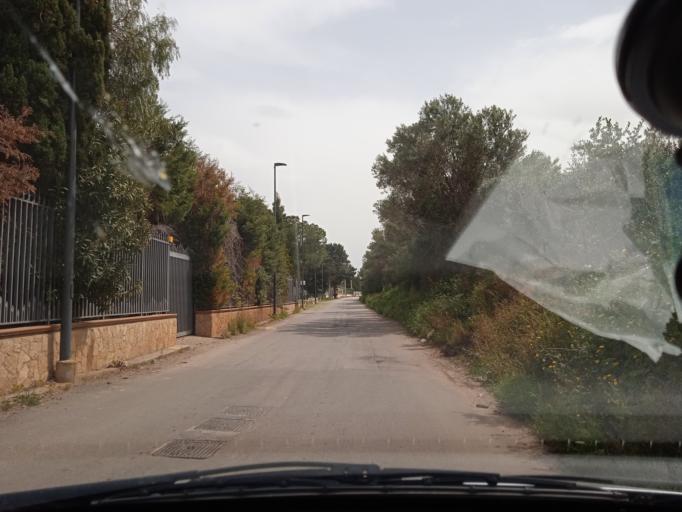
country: IT
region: Sicily
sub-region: Palermo
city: Torre Colonna-Sperone
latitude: 38.0234
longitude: 13.5794
